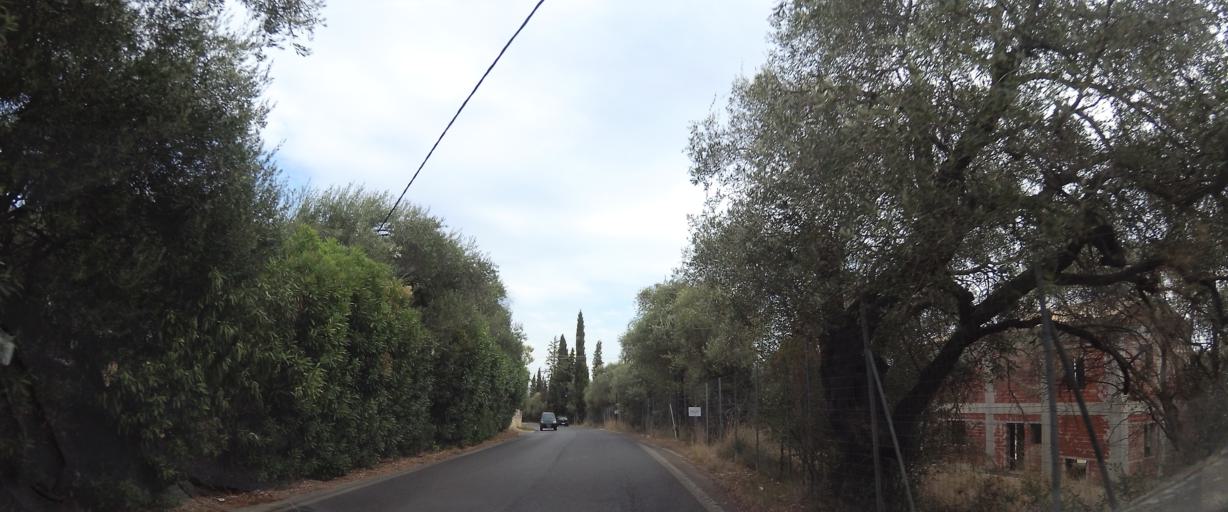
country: GR
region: Ionian Islands
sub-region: Nomos Kerkyras
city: Kontokali
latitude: 39.7243
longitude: 19.8850
